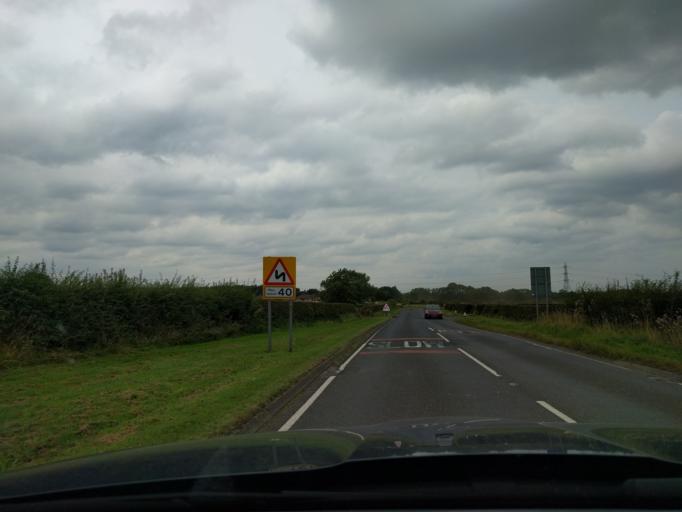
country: GB
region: England
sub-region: Northumberland
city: Stannington
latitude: 55.1318
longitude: -1.6458
